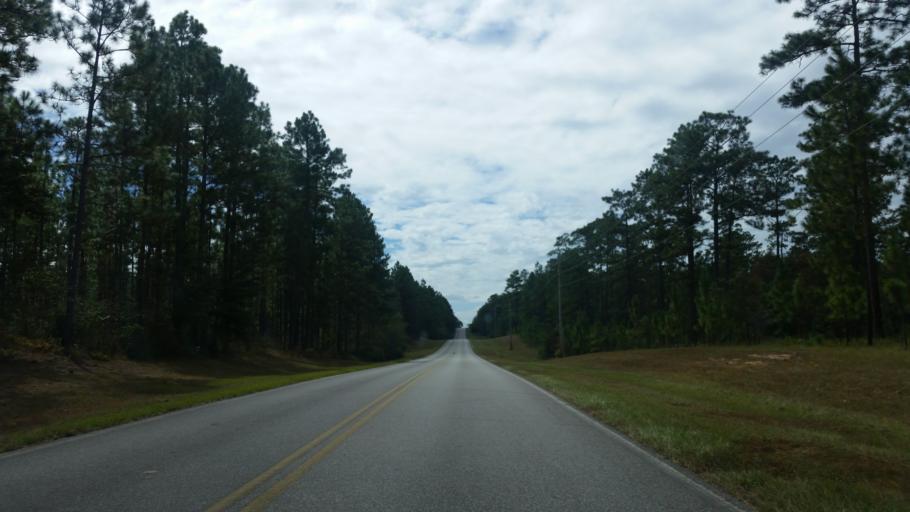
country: US
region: Florida
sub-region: Santa Rosa County
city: Point Baker
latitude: 30.8280
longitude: -86.9119
